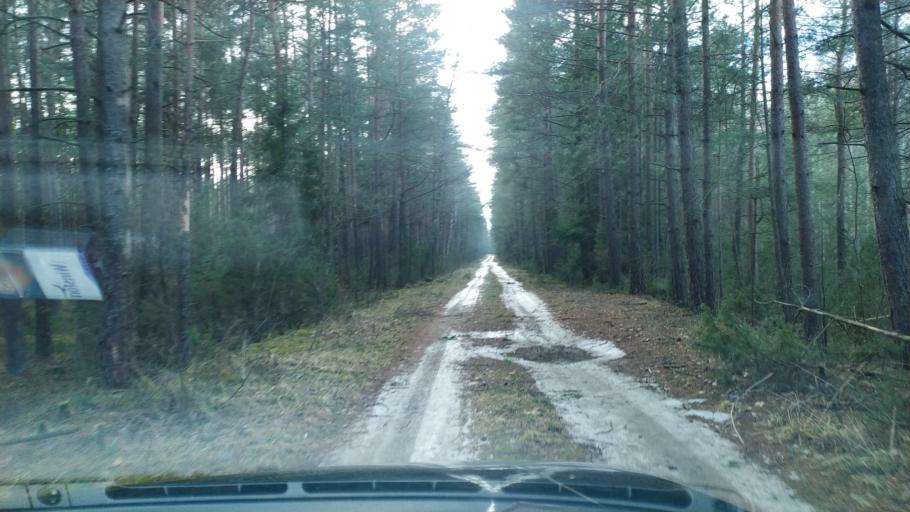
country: BY
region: Brest
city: Kamyanyets
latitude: 52.4295
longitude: 24.0003
